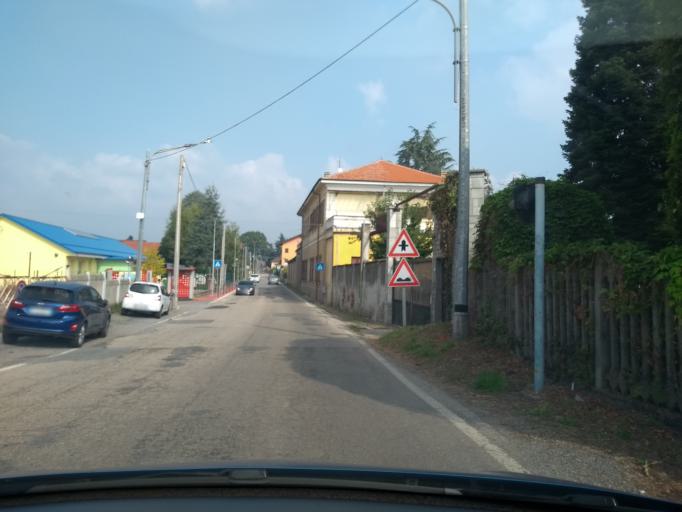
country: IT
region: Piedmont
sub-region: Provincia di Torino
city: Oglianico
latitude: 45.3363
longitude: 7.6915
